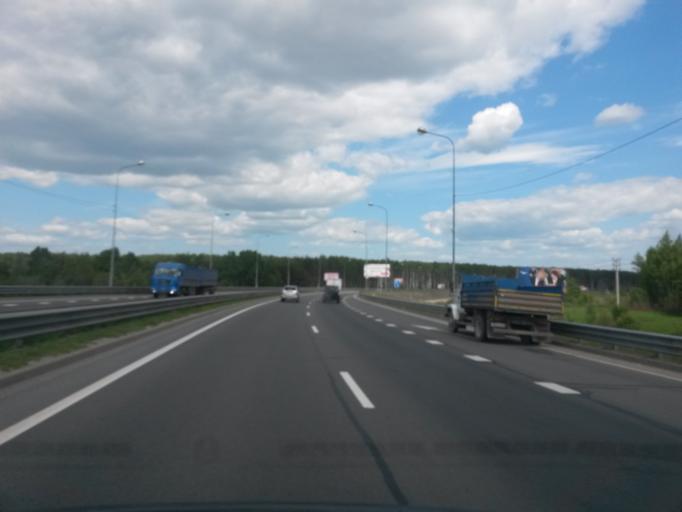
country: RU
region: Jaroslavl
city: Yaroslavl
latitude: 57.6819
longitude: 39.8728
